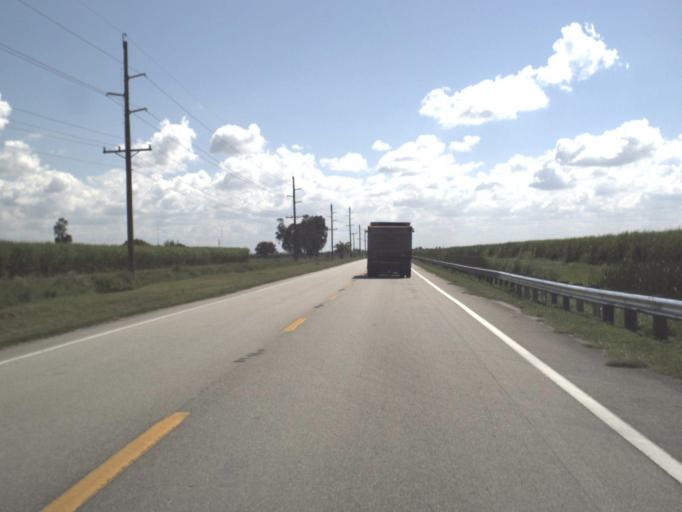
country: US
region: Florida
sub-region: Glades County
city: Moore Haven
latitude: 26.8683
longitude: -81.1227
